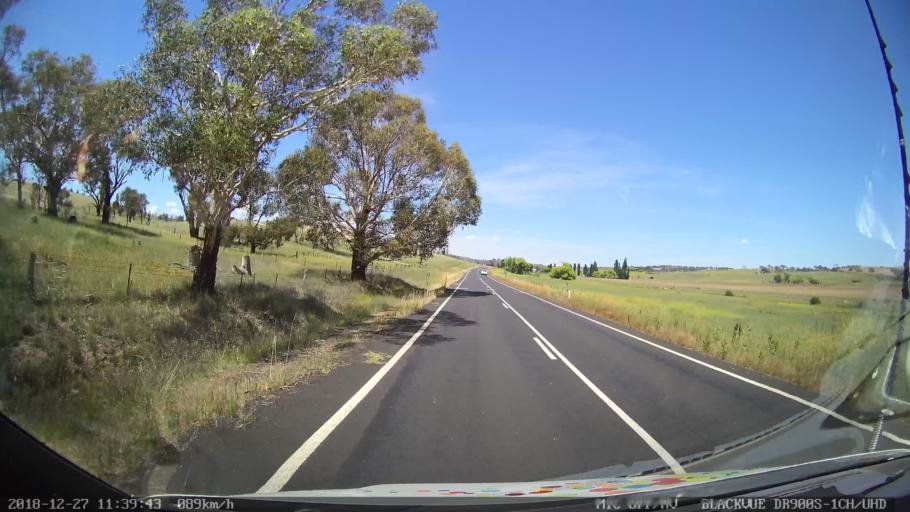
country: AU
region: New South Wales
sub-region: Bathurst Regional
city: Perthville
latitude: -33.5160
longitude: 149.4965
